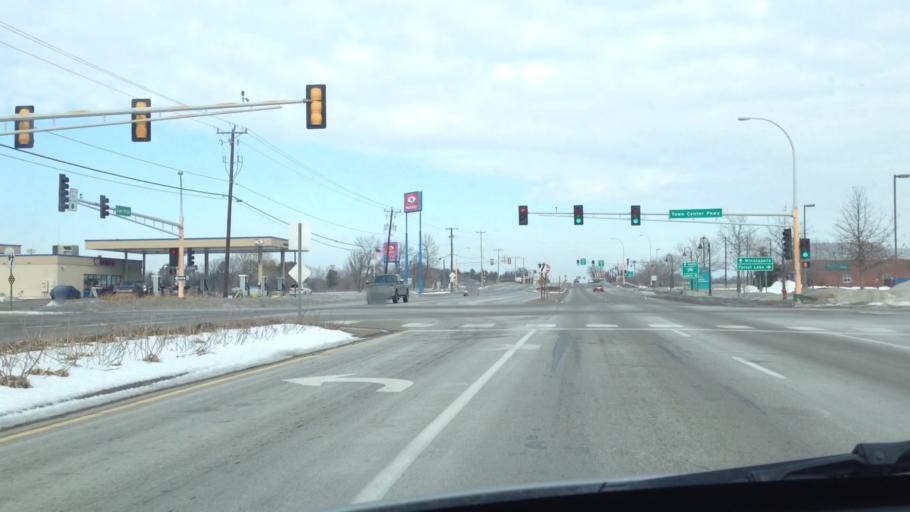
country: US
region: Minnesota
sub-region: Anoka County
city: Lino Lakes
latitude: 45.1771
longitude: -93.1149
